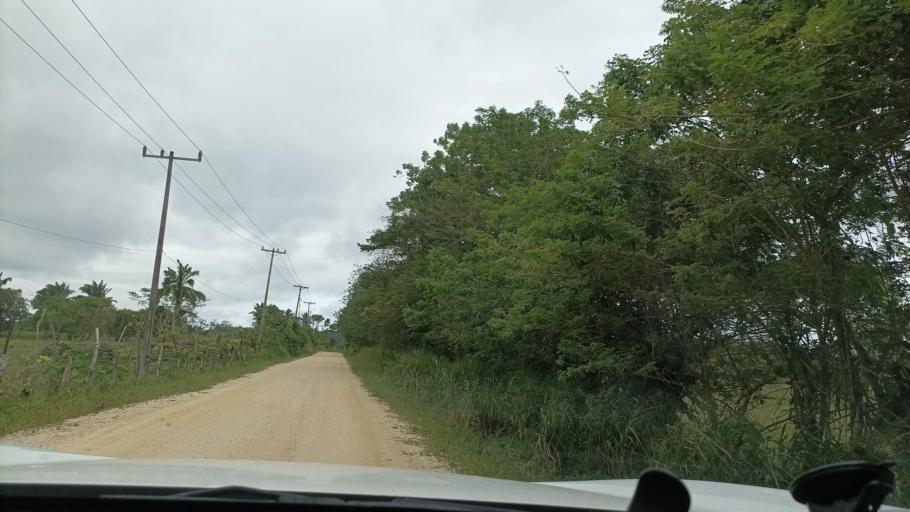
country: MX
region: Veracruz
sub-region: Moloacan
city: Cuichapa
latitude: 17.8261
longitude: -94.3541
